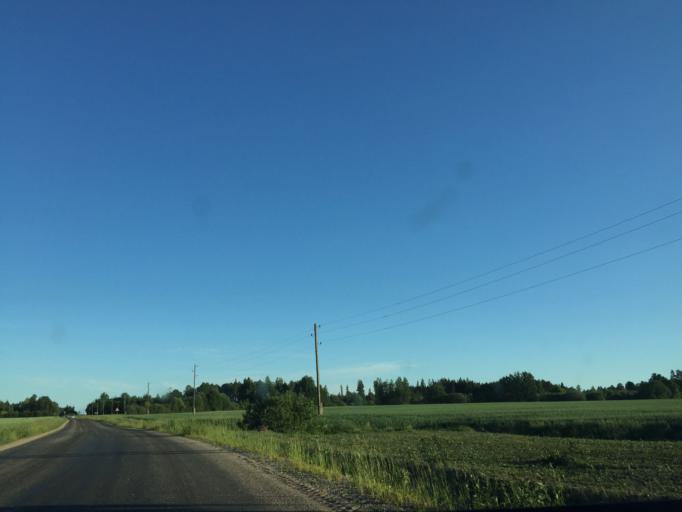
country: LV
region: Broceni
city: Broceni
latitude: 56.7186
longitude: 22.5006
